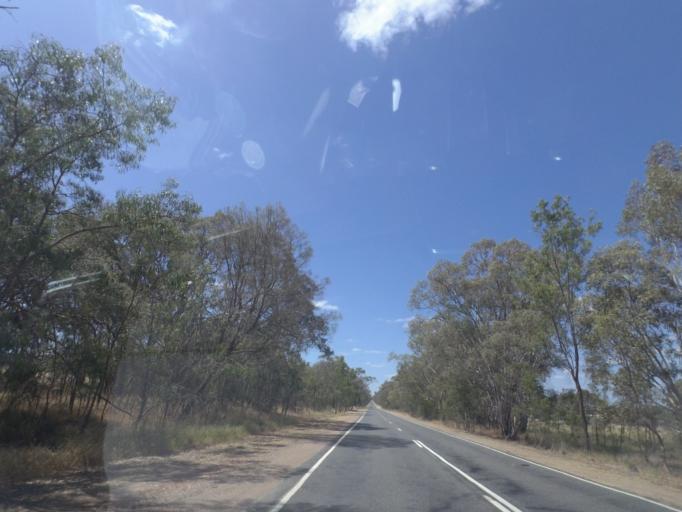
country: AU
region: Victoria
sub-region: Wangaratta
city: Wangaratta
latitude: -36.4417
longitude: 146.2451
